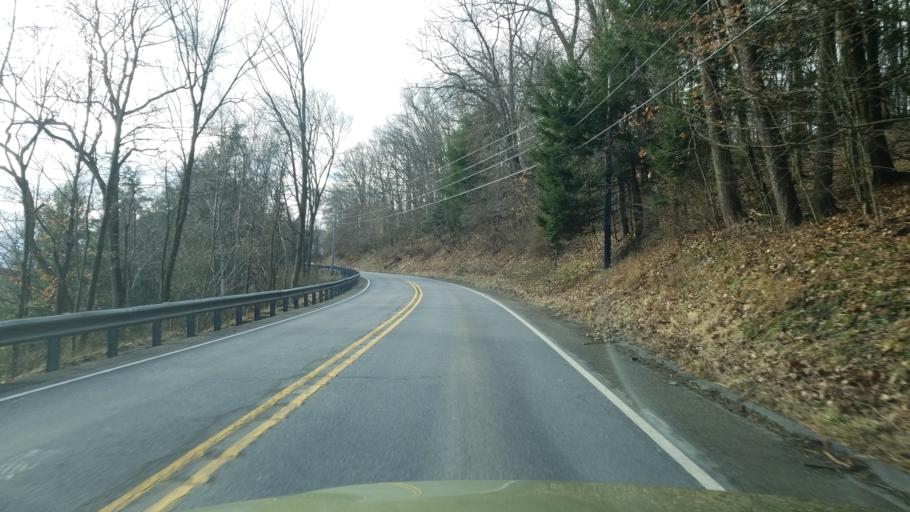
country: US
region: Pennsylvania
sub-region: Jefferson County
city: Albion
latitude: 40.9529
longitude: -78.9305
